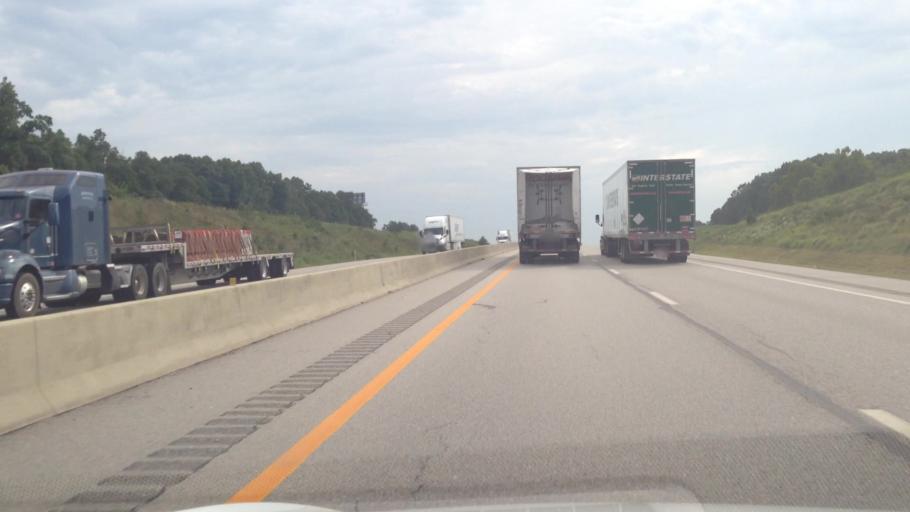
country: US
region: Kansas
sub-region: Cherokee County
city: Galena
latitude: 36.9833
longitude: -94.6344
